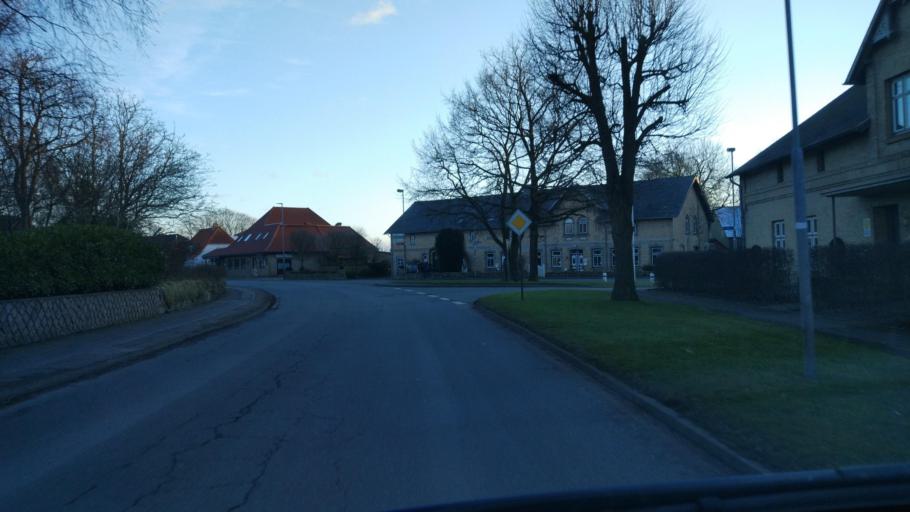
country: DE
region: Schleswig-Holstein
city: Hollingstedt
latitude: 54.4563
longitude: 9.3360
